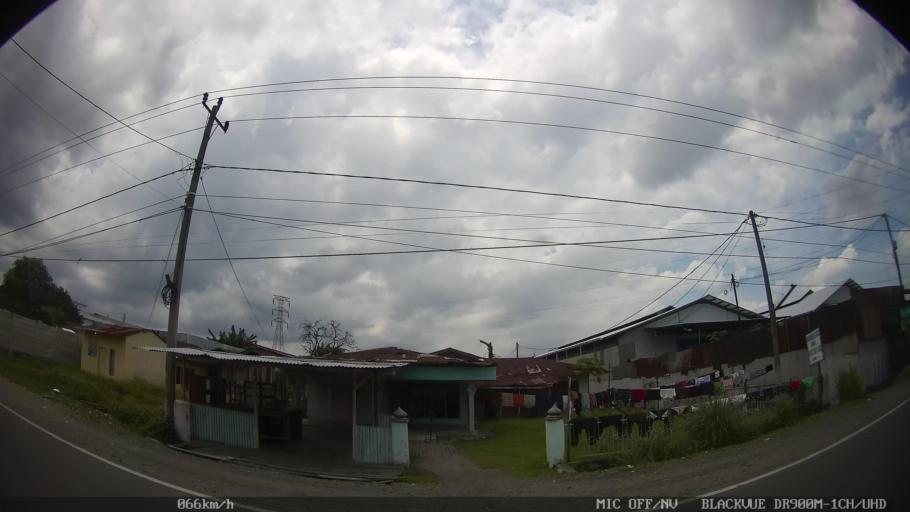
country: ID
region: North Sumatra
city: Medan
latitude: 3.6178
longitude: 98.6544
